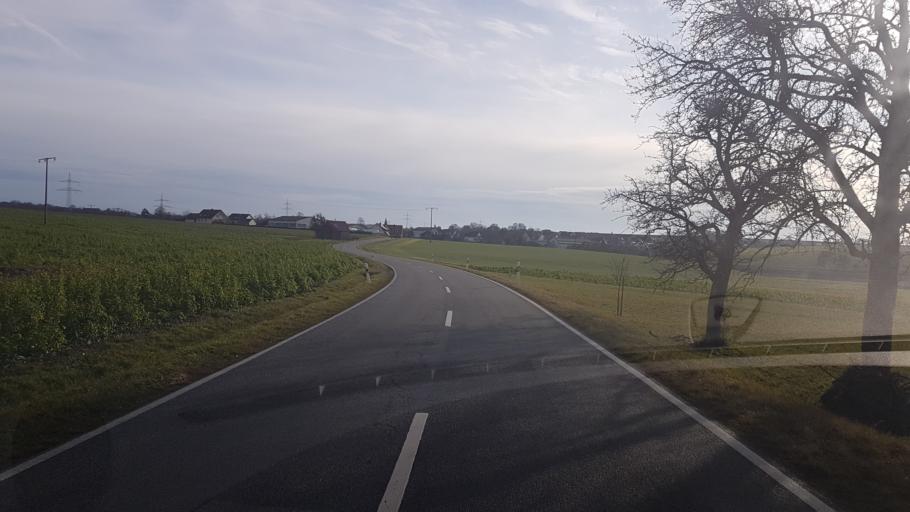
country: DE
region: Baden-Wuerttemberg
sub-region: Regierungsbezirk Stuttgart
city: Kupferzell
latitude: 49.2076
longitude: 9.7346
